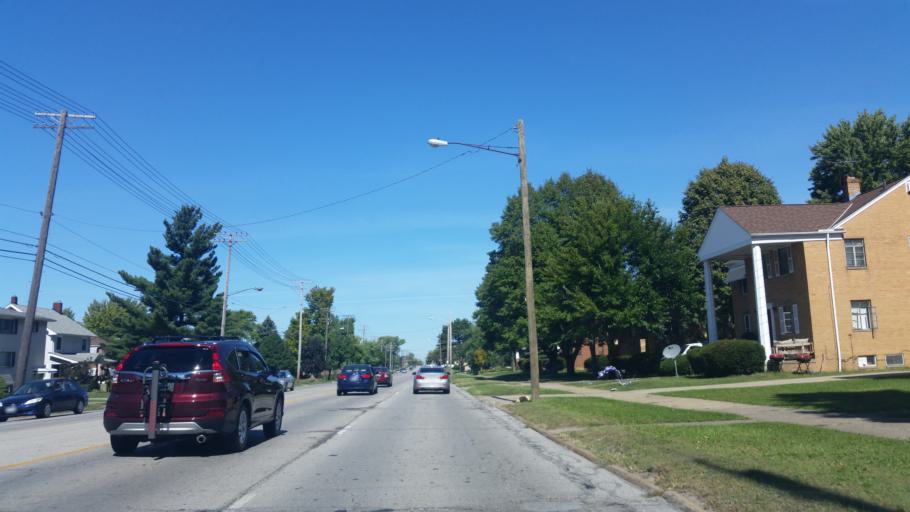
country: US
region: Ohio
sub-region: Cuyahoga County
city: Parma
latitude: 41.3878
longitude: -81.7345
